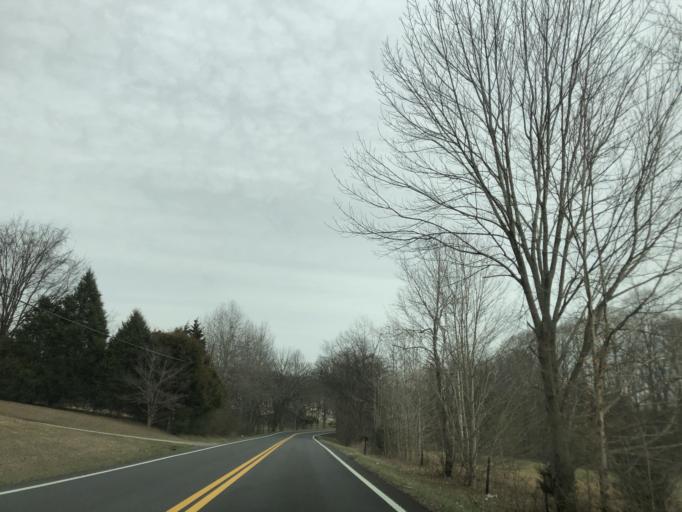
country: US
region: Tennessee
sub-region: Robertson County
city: Greenbrier
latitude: 36.4746
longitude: -86.7471
